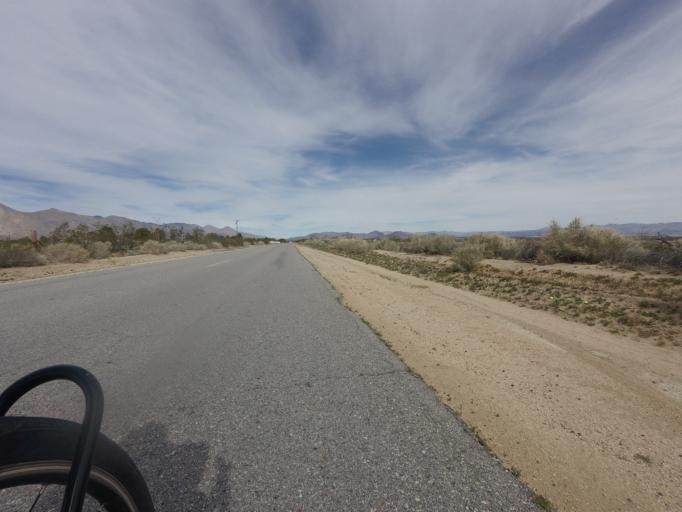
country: US
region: California
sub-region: Kern County
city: Inyokern
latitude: 35.7570
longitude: -117.8450
